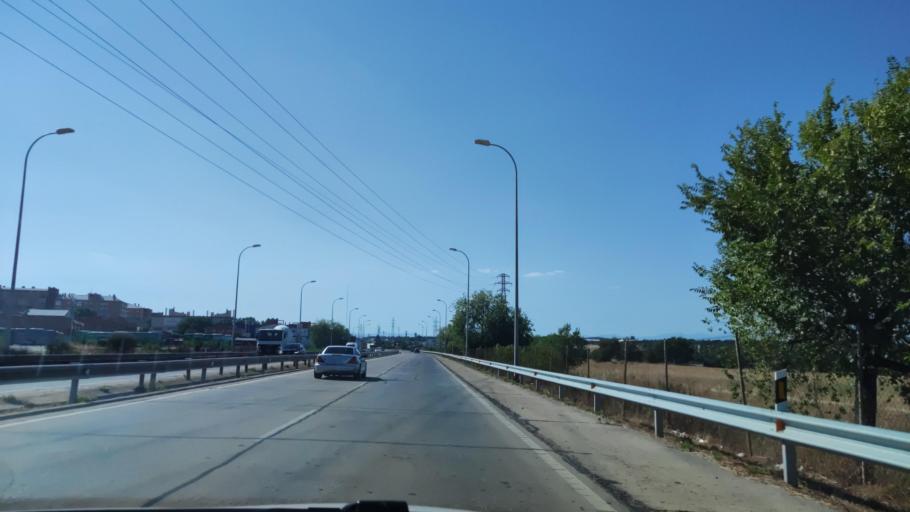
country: ES
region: Madrid
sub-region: Provincia de Madrid
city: Alcorcon
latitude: 40.3510
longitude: -3.7950
